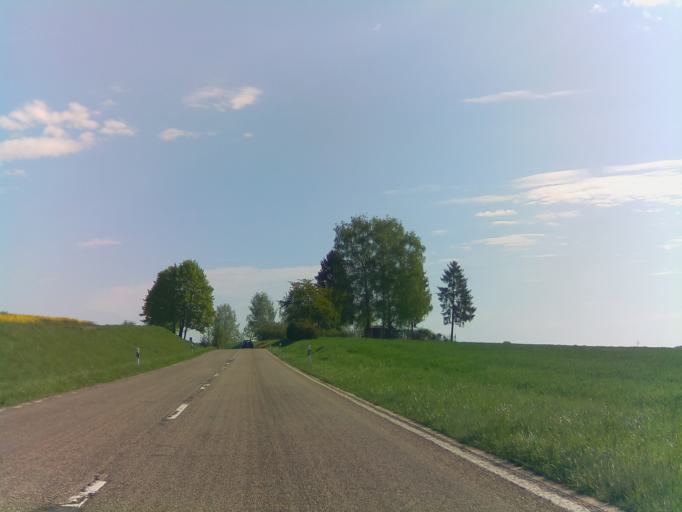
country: DE
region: Baden-Wuerttemberg
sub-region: Regierungsbezirk Stuttgart
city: Motzingen
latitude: 48.4950
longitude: 8.7684
